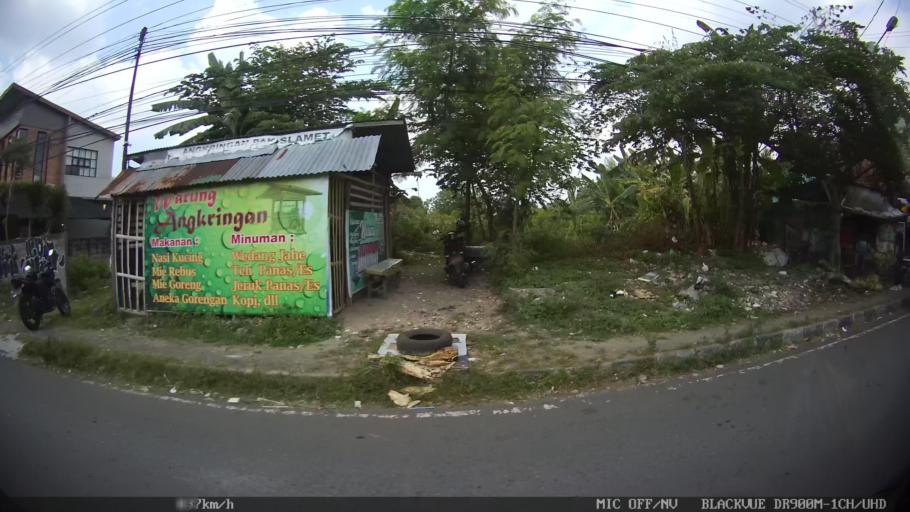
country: ID
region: Daerah Istimewa Yogyakarta
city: Yogyakarta
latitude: -7.8151
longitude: 110.4022
